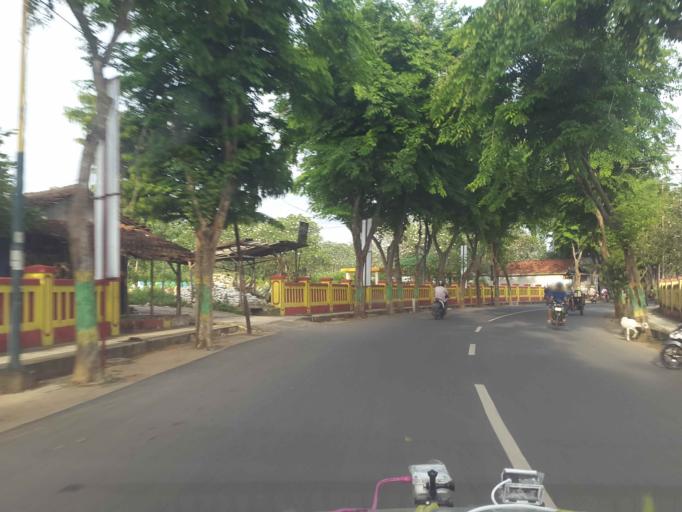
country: ID
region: East Java
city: Senmasen
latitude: -7.0004
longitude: 113.8629
